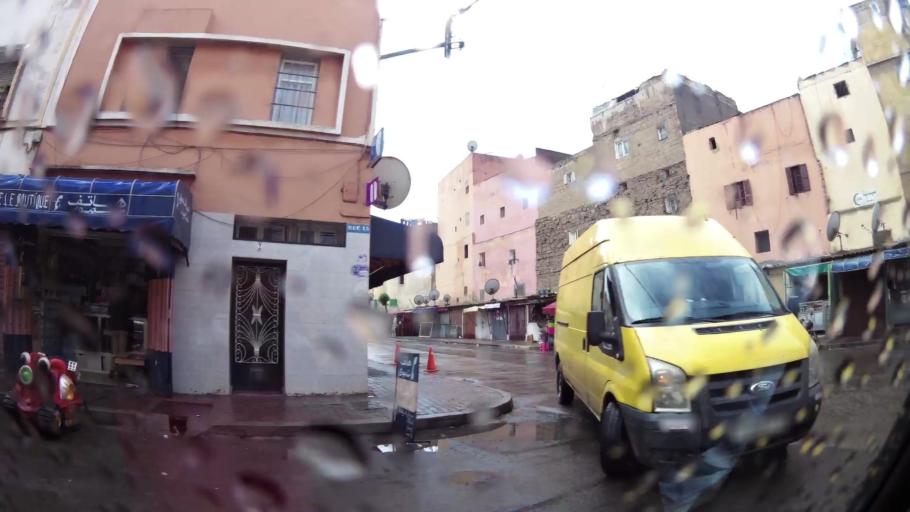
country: MA
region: Grand Casablanca
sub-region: Casablanca
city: Casablanca
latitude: 33.5694
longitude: -7.5943
